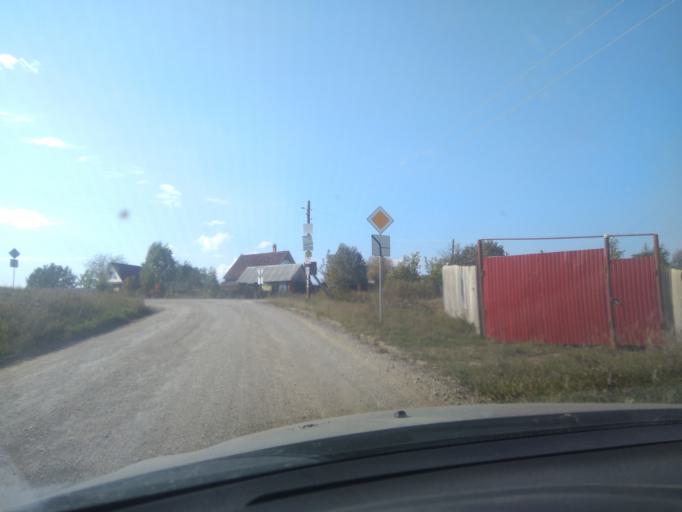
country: RU
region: Sverdlovsk
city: Pokrovskoye
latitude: 56.4366
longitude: 61.5899
